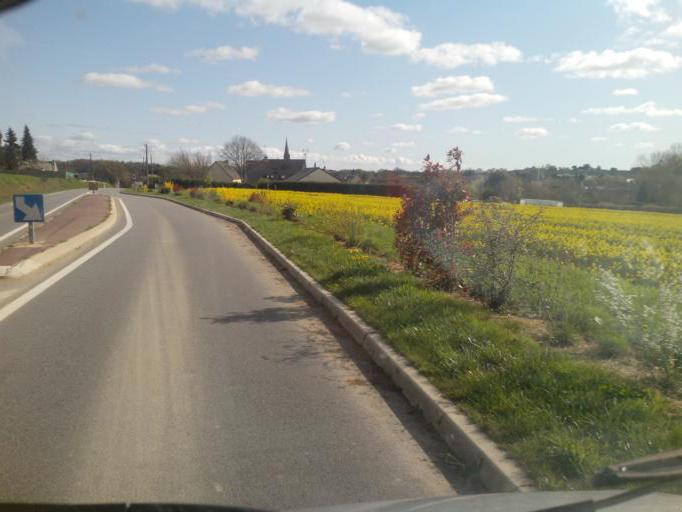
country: FR
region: Brittany
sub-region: Departement d'Ille-et-Vilaine
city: Maure-de-Bretagne
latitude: 47.8971
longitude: -1.9898
